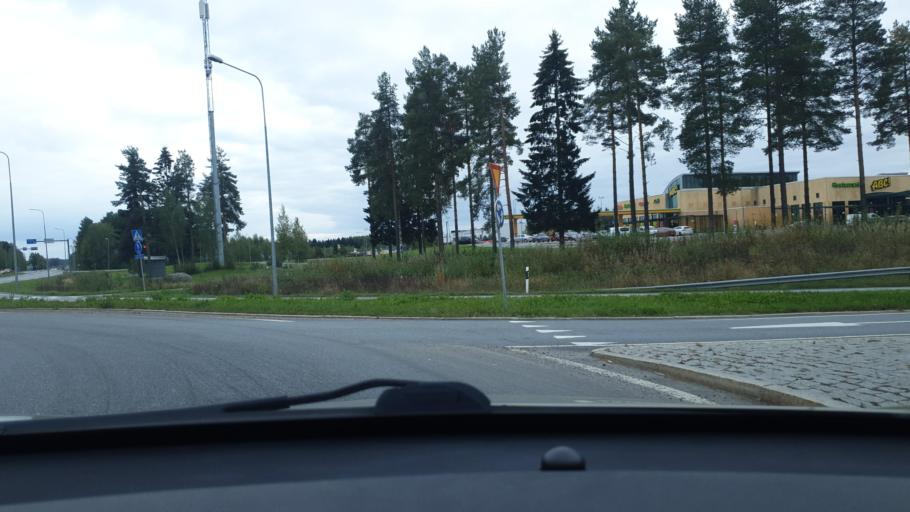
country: FI
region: Ostrobothnia
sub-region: Vaasa
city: Ristinummi
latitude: 63.0544
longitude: 21.7191
